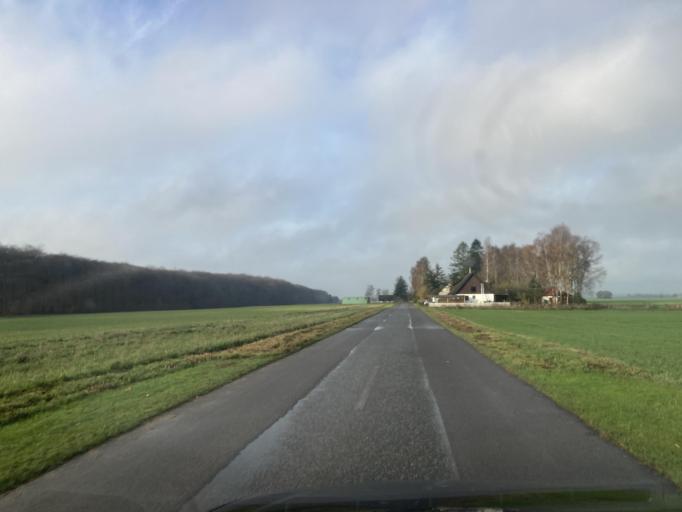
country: DK
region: Zealand
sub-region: Lolland Kommune
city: Rodby
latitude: 54.7940
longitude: 11.3519
